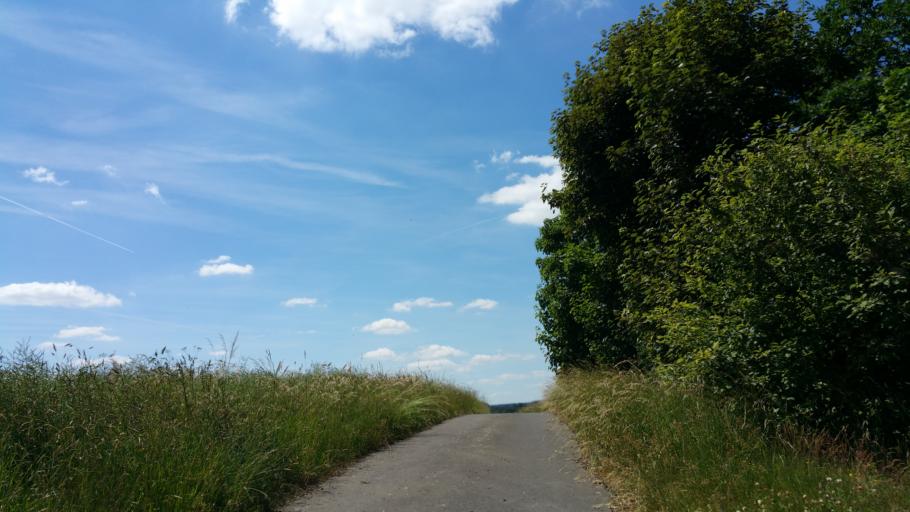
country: DE
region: Bavaria
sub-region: Upper Franconia
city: Schwarzenbach an der Saale
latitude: 50.2263
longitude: 11.9170
